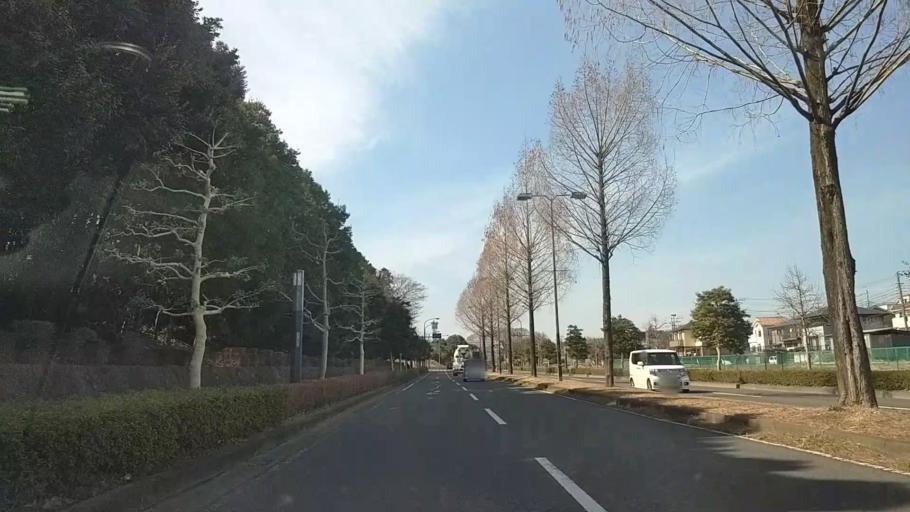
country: JP
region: Kanagawa
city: Fujisawa
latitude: 35.3917
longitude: 139.4269
